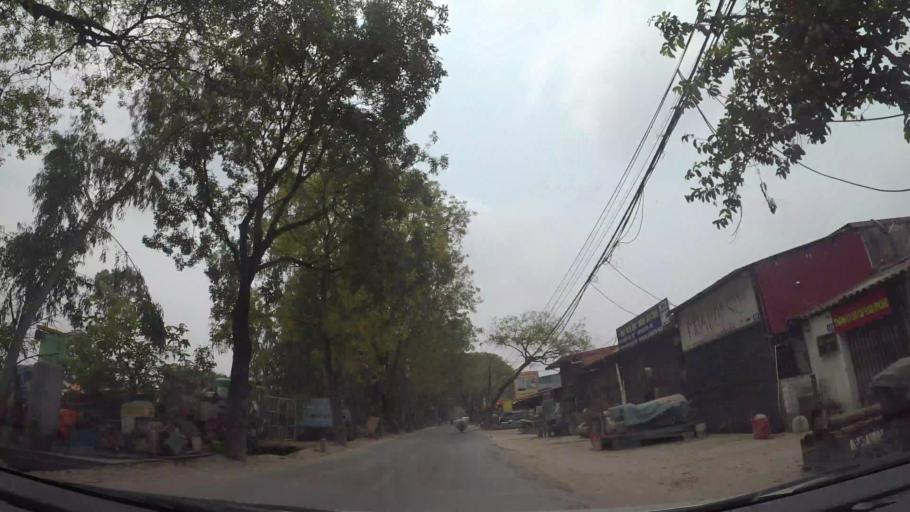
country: VN
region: Ha Noi
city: Cau Dien
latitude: 21.0177
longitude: 105.7447
